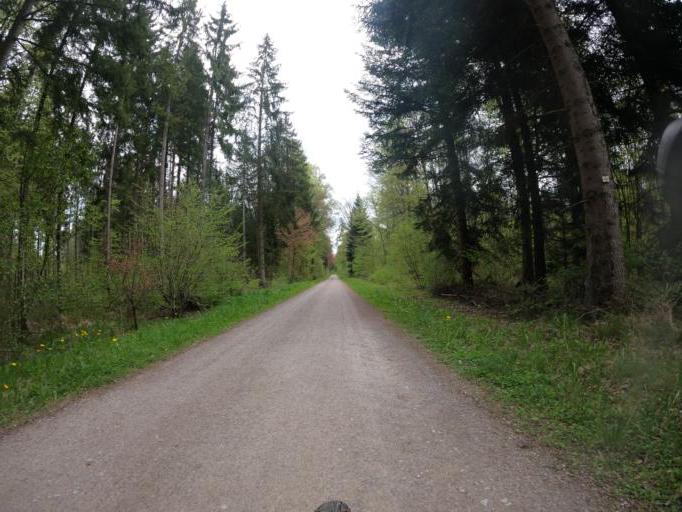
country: DE
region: Baden-Wuerttemberg
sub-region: Karlsruhe Region
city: Rohrdorf
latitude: 48.5511
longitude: 8.6873
